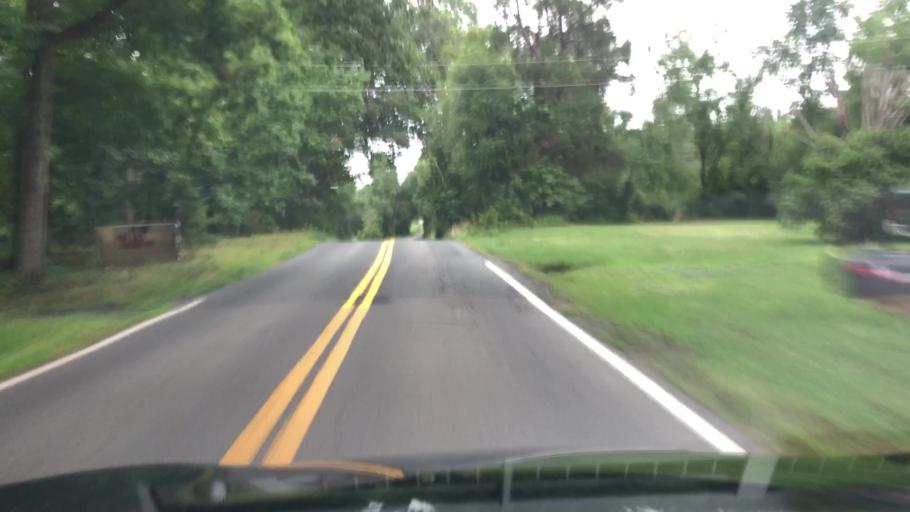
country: US
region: Virginia
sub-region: Fauquier County
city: Bealeton
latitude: 38.4945
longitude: -77.5966
